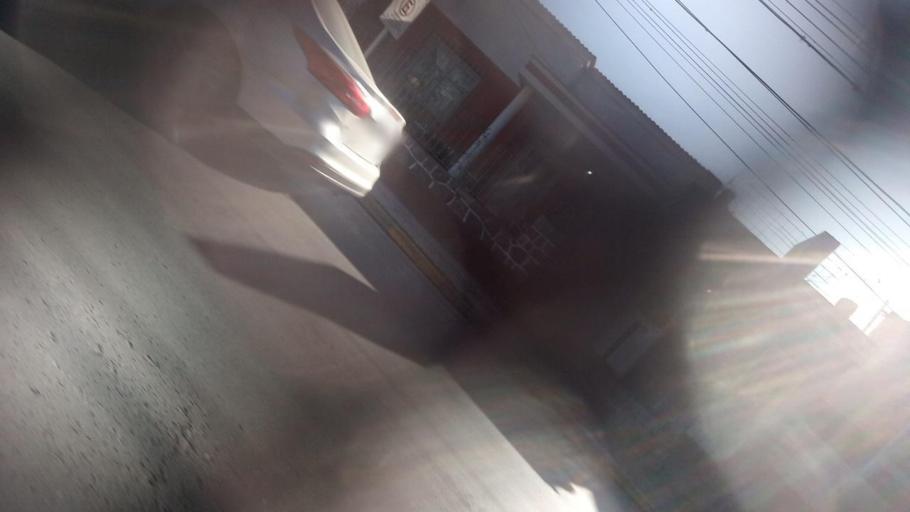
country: AR
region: Jujuy
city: San Salvador de Jujuy
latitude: -24.1708
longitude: -65.3109
